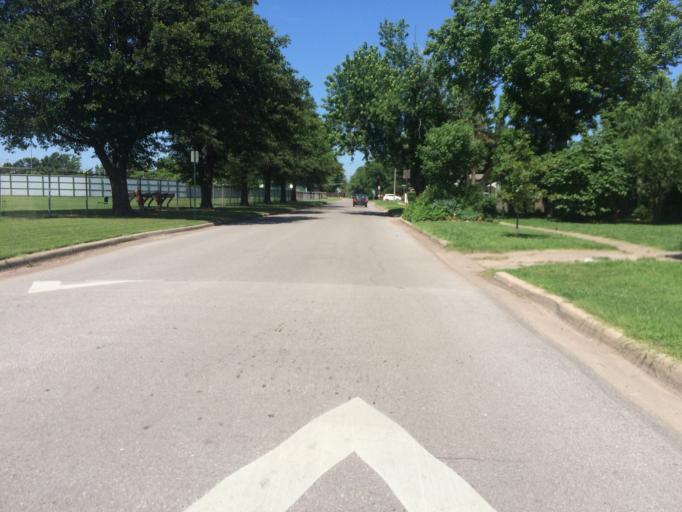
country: US
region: Oklahoma
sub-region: Cleveland County
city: Norman
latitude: 35.2222
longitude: -97.4564
